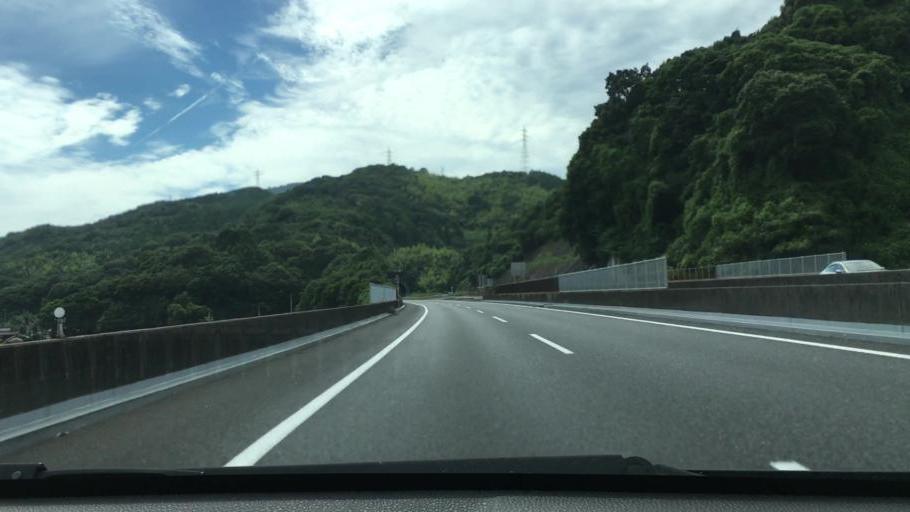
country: JP
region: Yamaguchi
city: Hofu
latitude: 34.0724
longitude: 131.6773
